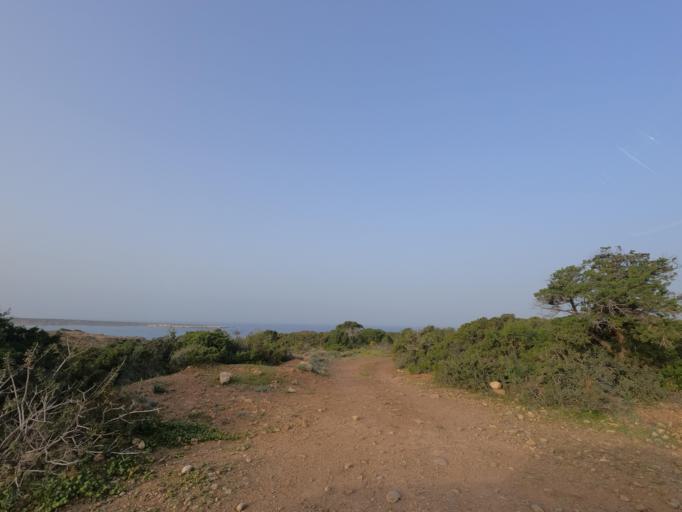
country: CY
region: Pafos
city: Pegeia
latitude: 34.9703
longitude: 32.3124
